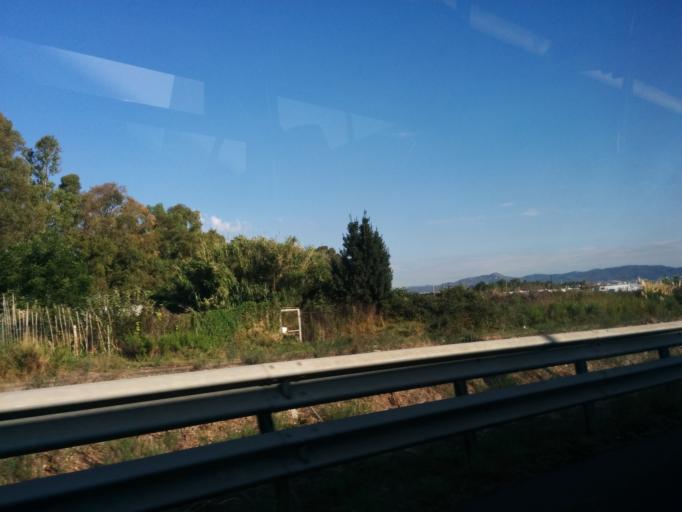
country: ES
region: Catalonia
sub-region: Provincia de Barcelona
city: El Prat de Llobregat
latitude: 41.3135
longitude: 2.0680
